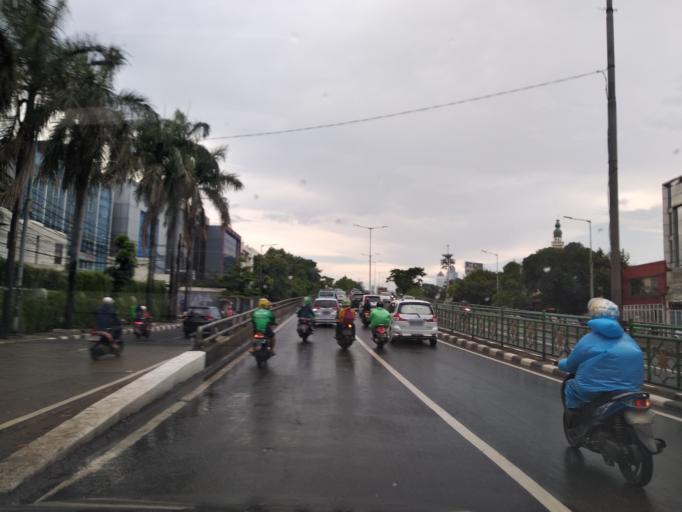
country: ID
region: Jakarta Raya
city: Jakarta
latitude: -6.2253
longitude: 106.8611
